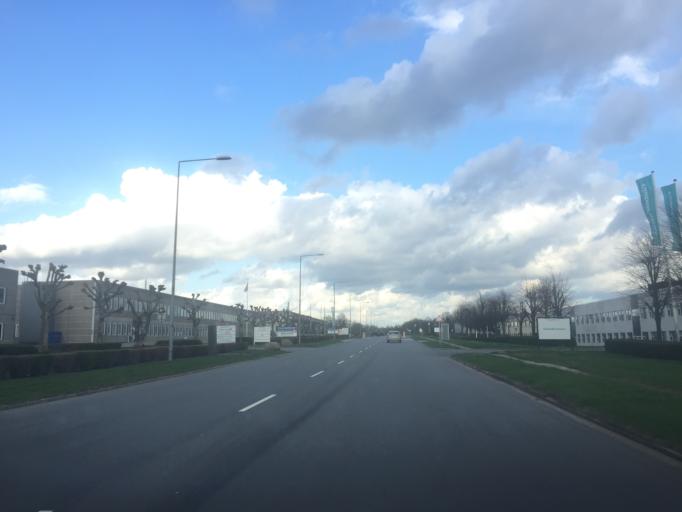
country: DK
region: Capital Region
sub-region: Hoje-Taastrup Kommune
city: Taastrup
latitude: 55.6628
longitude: 12.3001
